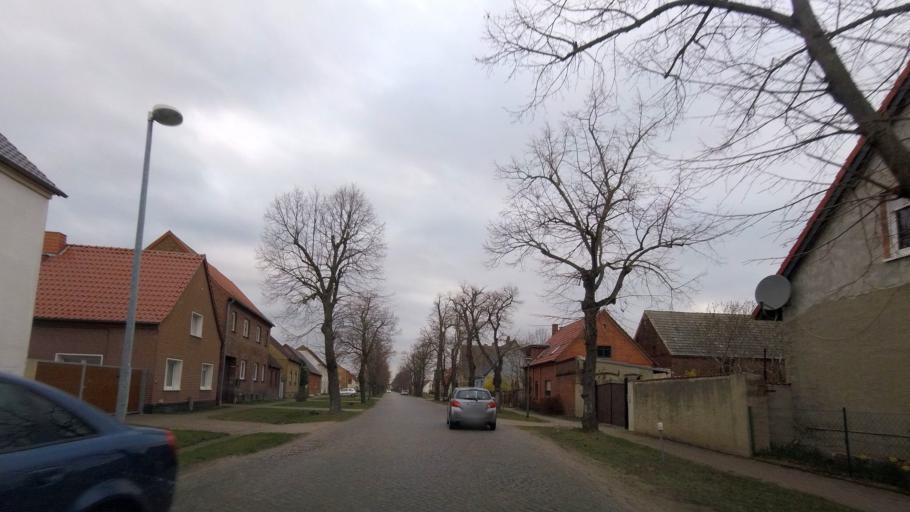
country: DE
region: Saxony-Anhalt
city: Bergwitz
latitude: 51.7933
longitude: 12.5974
